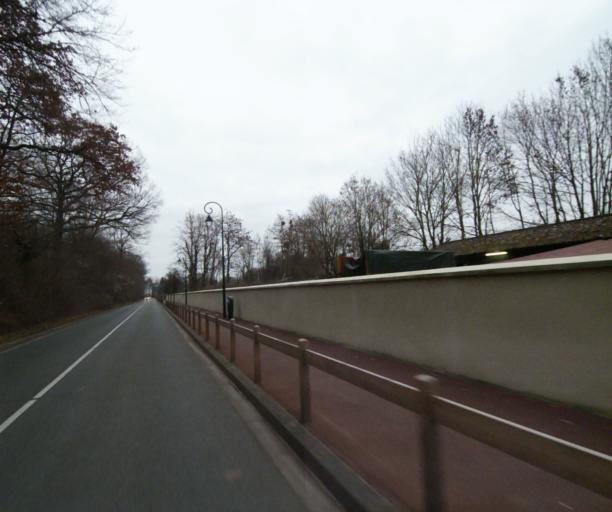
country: FR
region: Ile-de-France
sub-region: Departement des Hauts-de-Seine
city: Vaucresson
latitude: 48.8465
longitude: 2.1651
